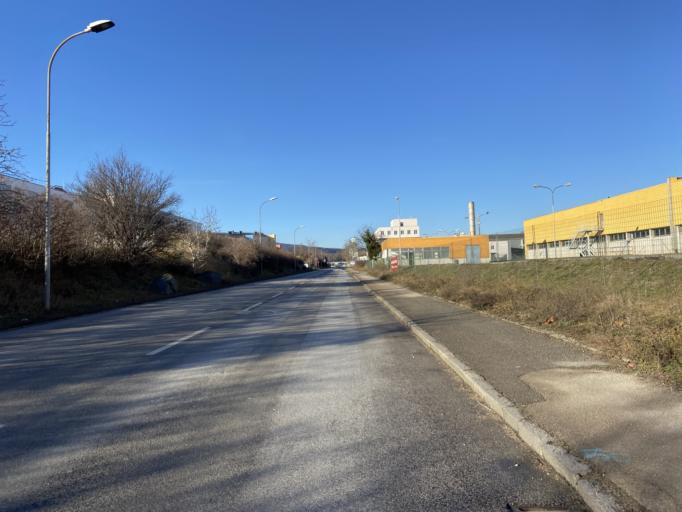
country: AT
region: Lower Austria
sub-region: Politischer Bezirk Modling
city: Neu-Guntramsdorf
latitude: 48.0675
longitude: 16.3221
